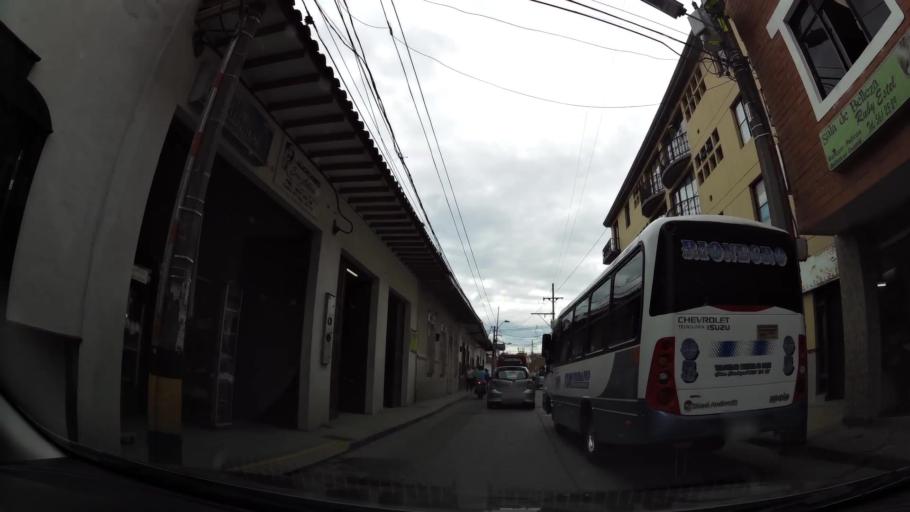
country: CO
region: Antioquia
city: Rionegro
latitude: 6.1543
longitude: -75.3709
